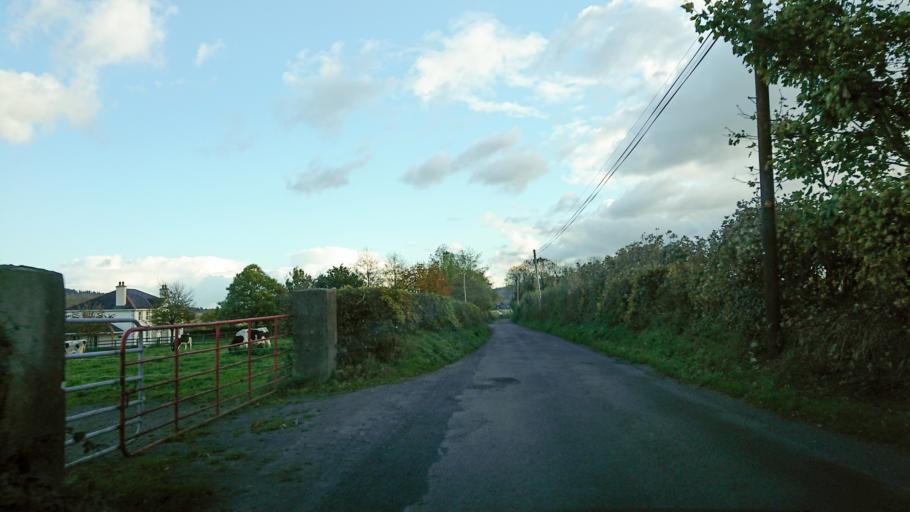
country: IE
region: Leinster
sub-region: Kilkenny
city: Graiguenamanagh
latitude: 52.4779
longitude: -6.9139
